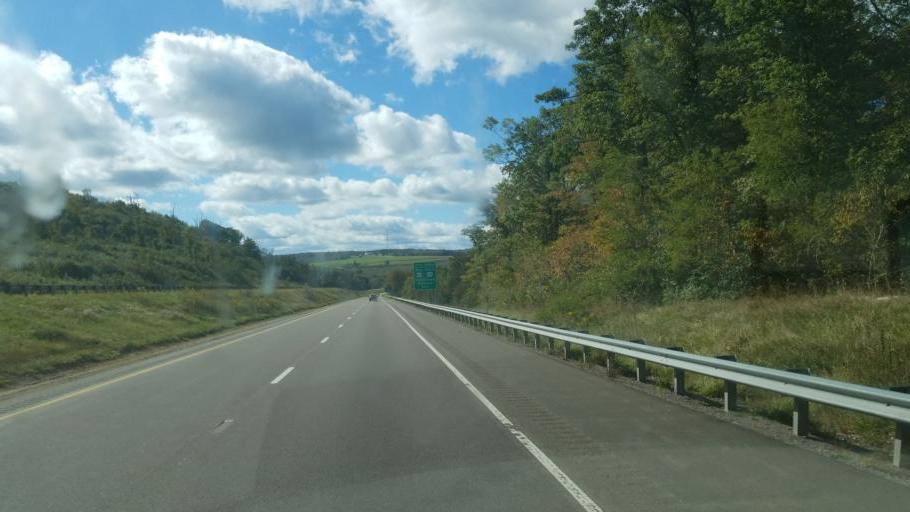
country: US
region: Pennsylvania
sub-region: Somerset County
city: Meyersdale
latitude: 39.6803
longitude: -79.2243
